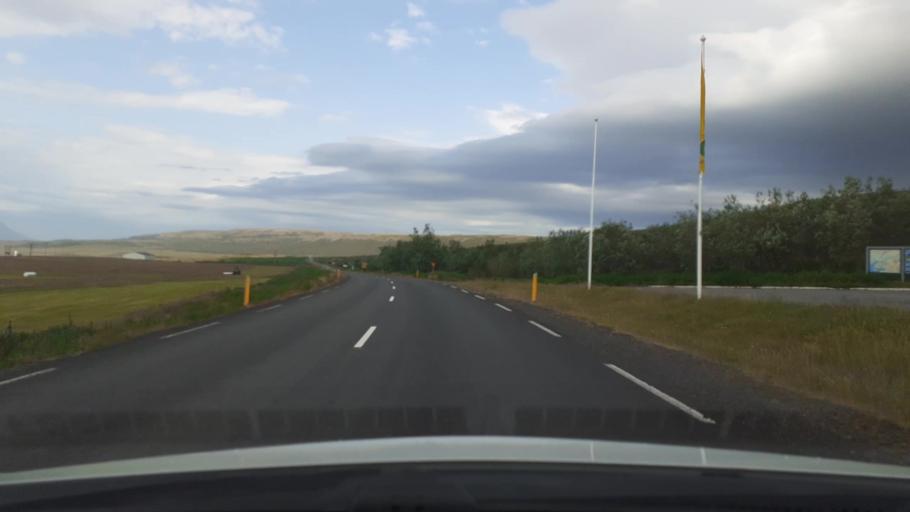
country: IS
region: Capital Region
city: Mosfellsbaer
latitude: 64.4100
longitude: -21.5974
